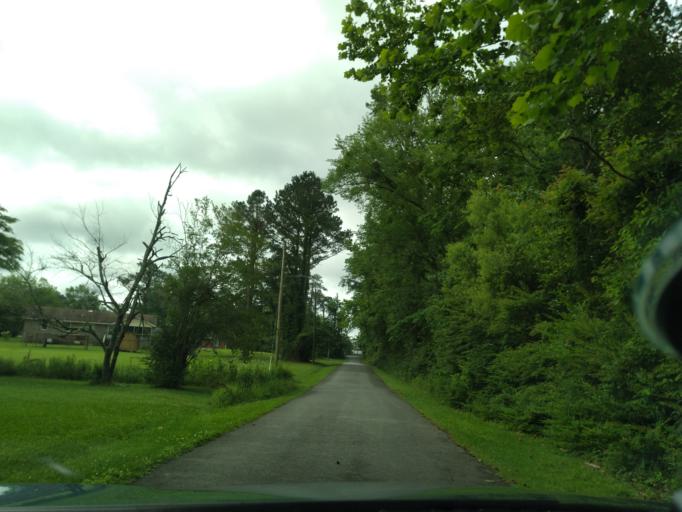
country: US
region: North Carolina
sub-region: Washington County
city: Plymouth
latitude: 35.8745
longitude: -76.7384
